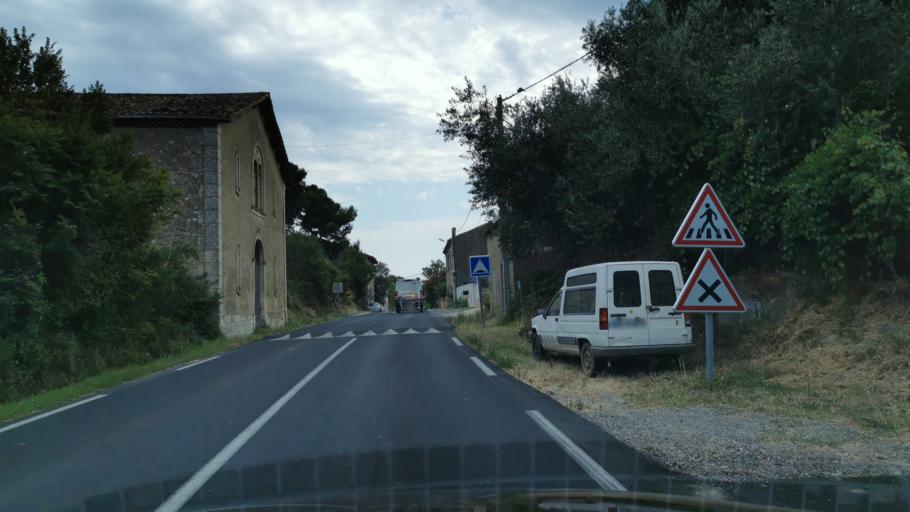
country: FR
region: Languedoc-Roussillon
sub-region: Departement de l'Herault
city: Capestang
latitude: 43.2955
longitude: 3.0299
